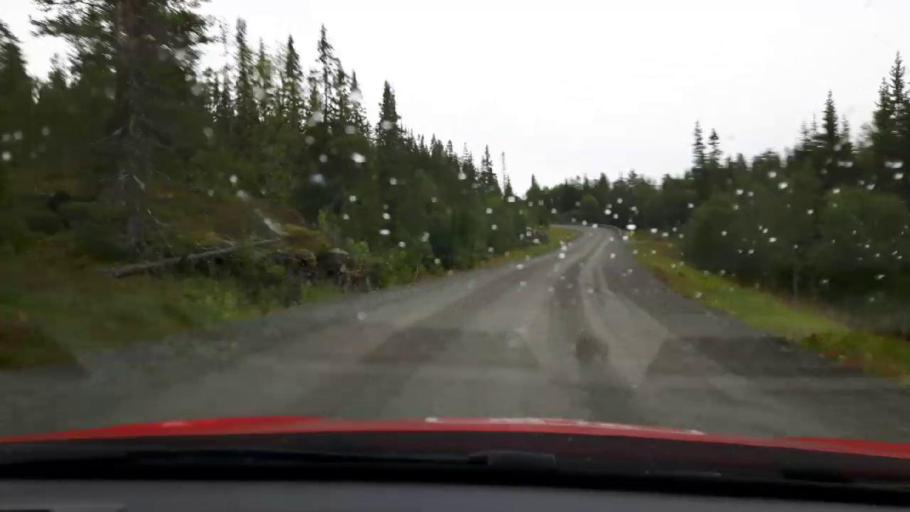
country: NO
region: Nord-Trondelag
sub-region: Meraker
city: Meraker
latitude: 63.6451
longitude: 12.2663
